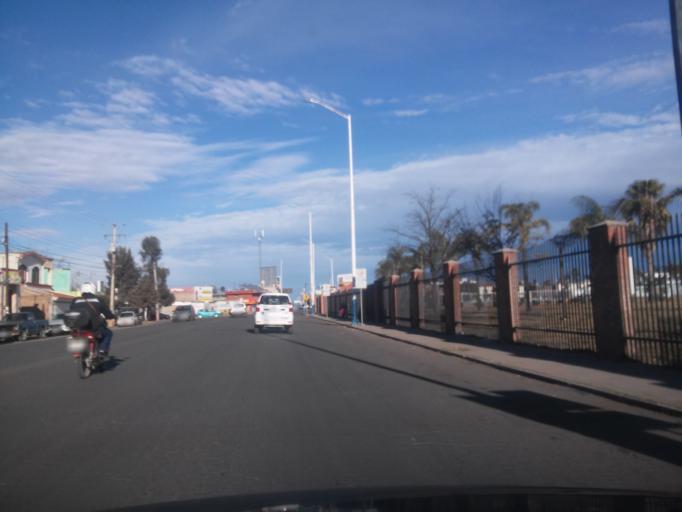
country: MX
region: Durango
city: Victoria de Durango
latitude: 24.0058
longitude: -104.6459
